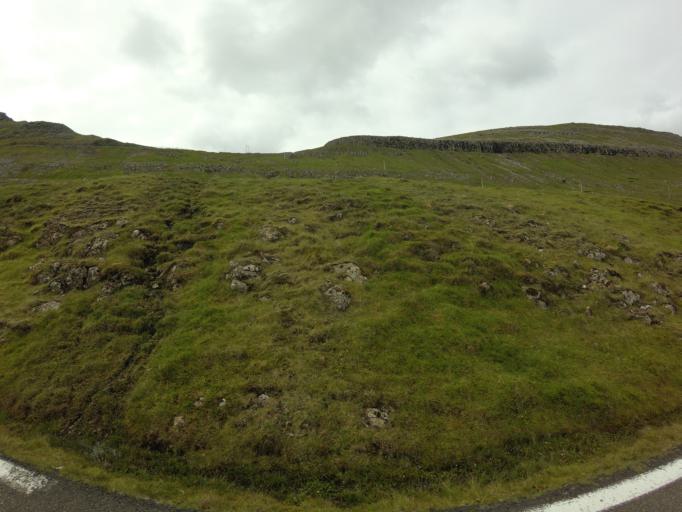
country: FO
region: Suduroy
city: Tvoroyri
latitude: 61.5268
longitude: -6.8345
